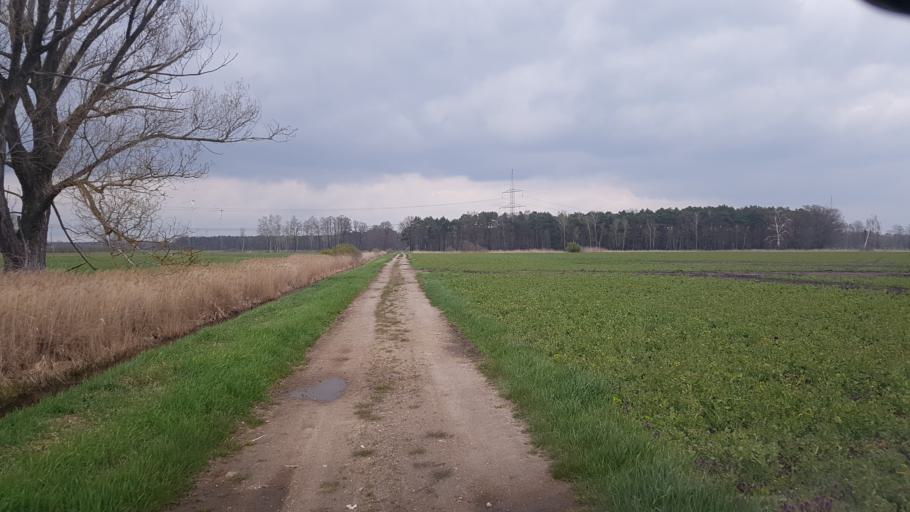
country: DE
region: Brandenburg
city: Sallgast
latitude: 51.6266
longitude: 13.8750
